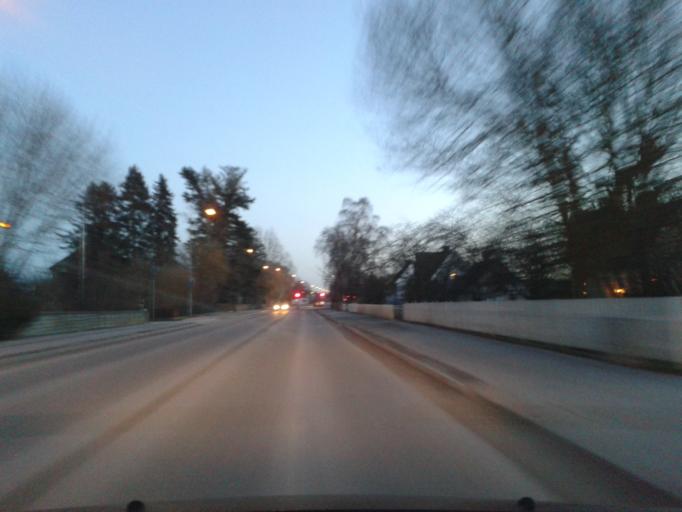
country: SE
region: Gotland
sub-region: Gotland
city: Visby
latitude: 57.6340
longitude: 18.3088
